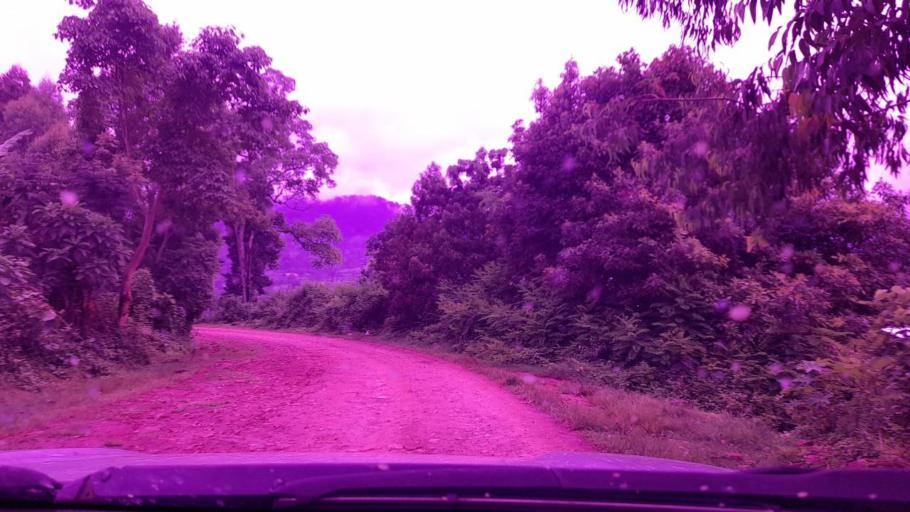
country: ET
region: Southern Nations, Nationalities, and People's Region
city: Bonga
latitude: 7.5516
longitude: 35.8441
